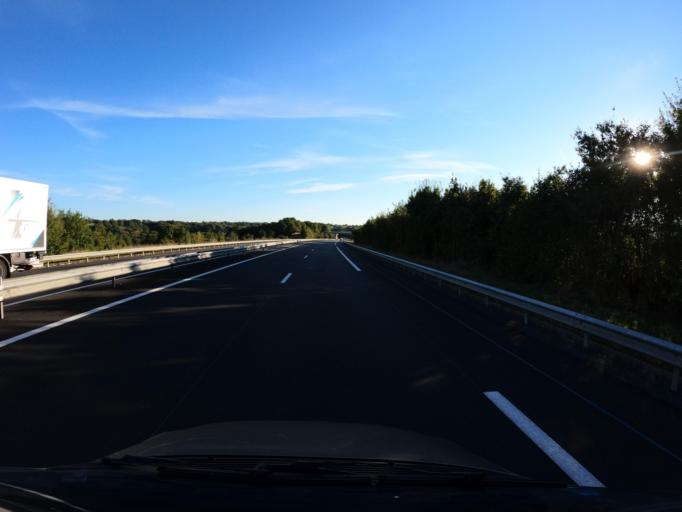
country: FR
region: Pays de la Loire
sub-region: Departement de la Vendee
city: Saint-Laurent-sur-Sevre
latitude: 46.9725
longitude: -0.9179
